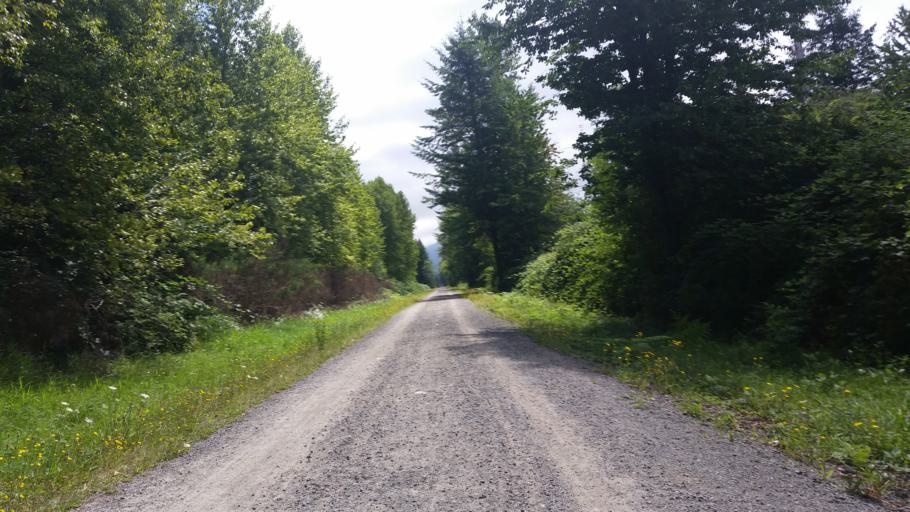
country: US
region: Washington
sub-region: King County
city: North Bend
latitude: 47.4891
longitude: -121.7680
